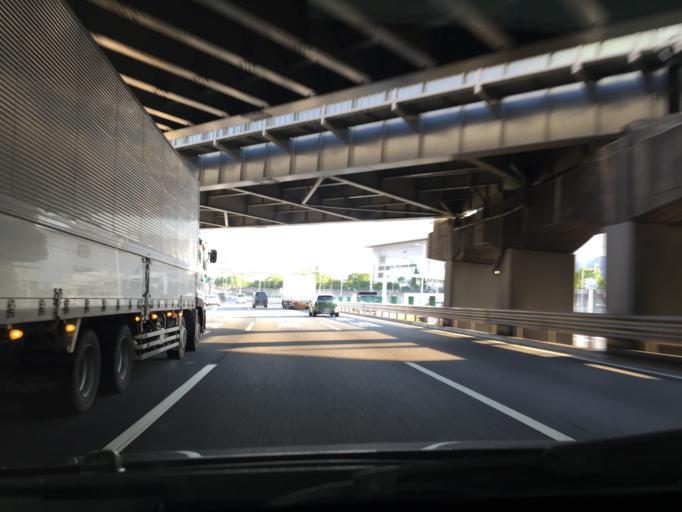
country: JP
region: Kanagawa
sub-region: Kawasaki-shi
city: Kawasaki
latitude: 35.6111
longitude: 139.7559
